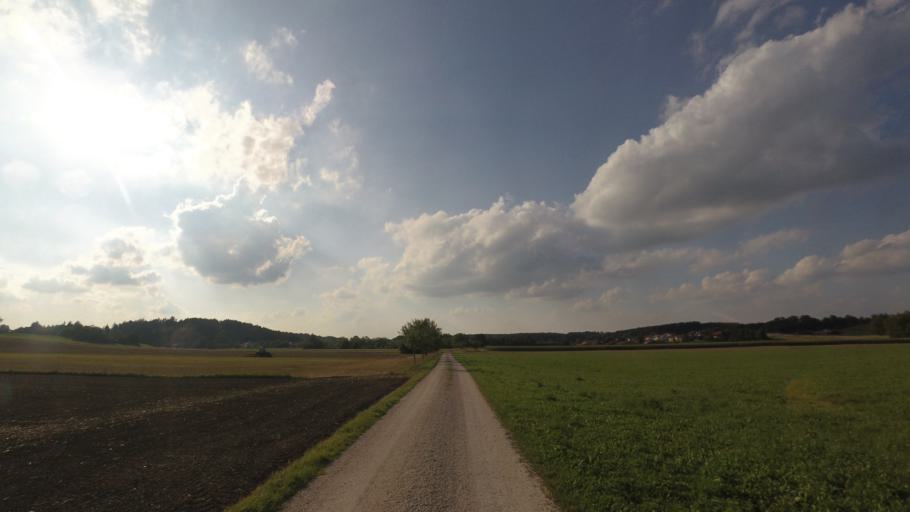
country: DE
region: Bavaria
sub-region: Upper Bavaria
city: Chieming
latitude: 47.9042
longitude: 12.5636
